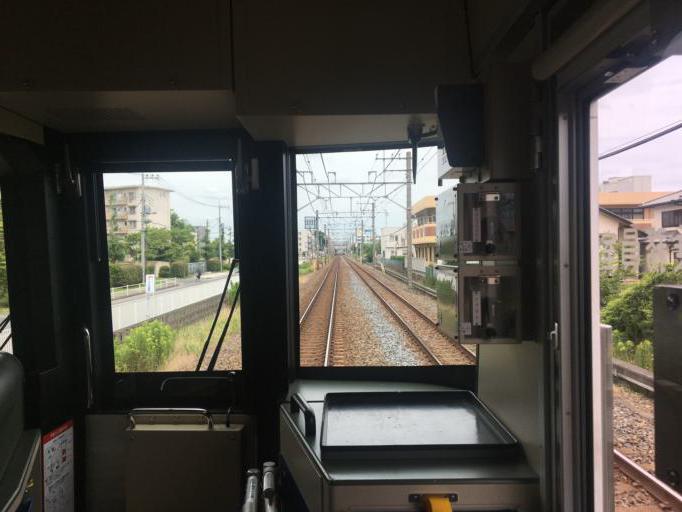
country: JP
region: Saitama
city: Kasukabe
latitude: 35.9440
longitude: 139.7722
